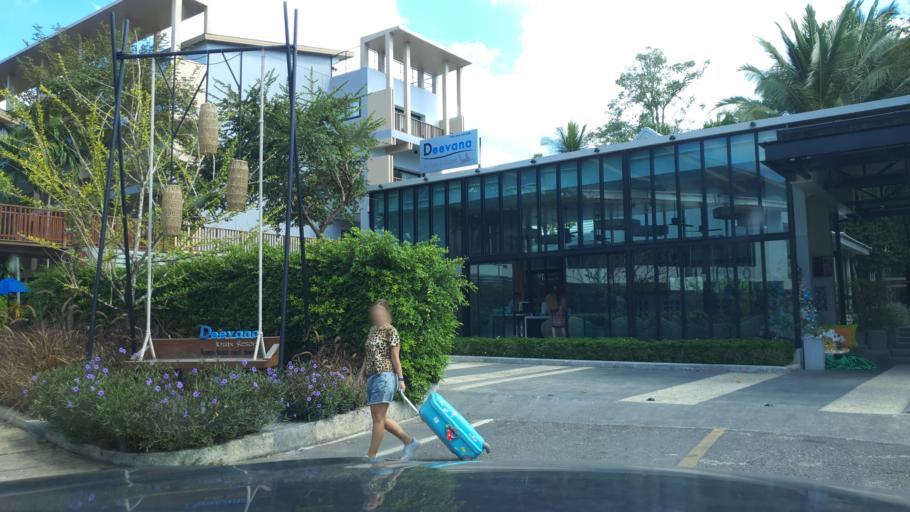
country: TH
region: Phangnga
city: Ban Ao Nang
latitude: 8.0422
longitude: 98.8182
